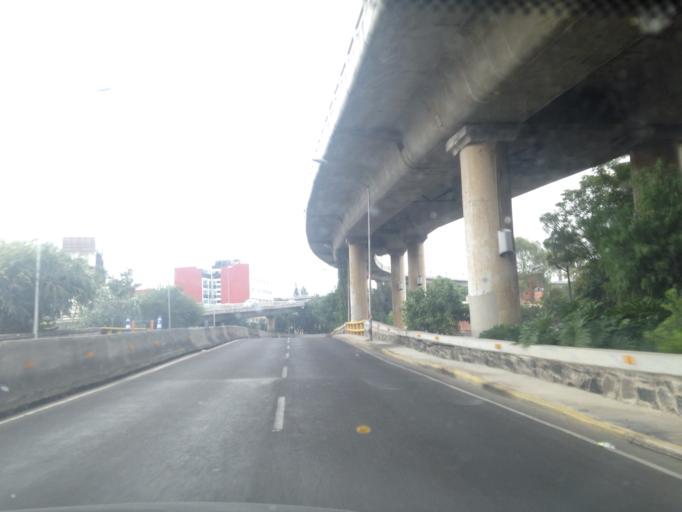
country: MX
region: Mexico City
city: Colonia del Valle
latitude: 19.3878
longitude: -99.1815
